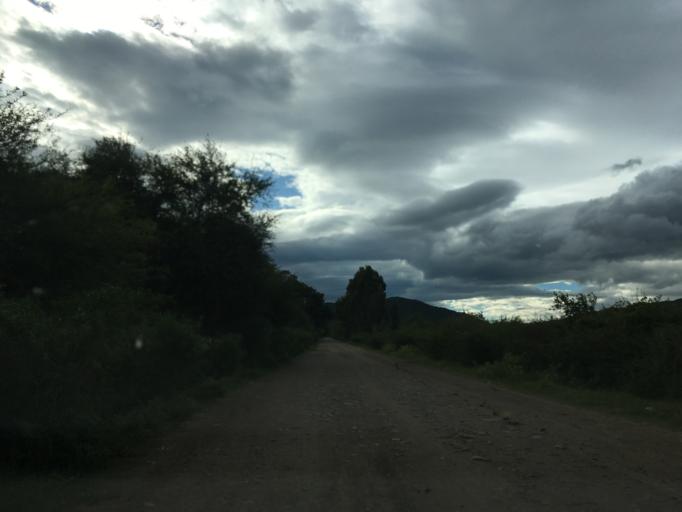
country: MX
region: Guanajuato
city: Iramuco
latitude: 19.9707
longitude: -100.9491
